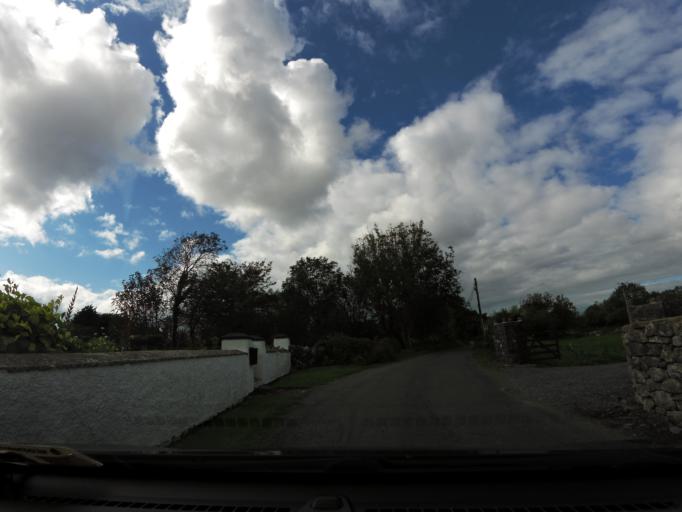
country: IE
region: Connaught
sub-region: County Galway
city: Moycullen
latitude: 53.3540
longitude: -9.1623
